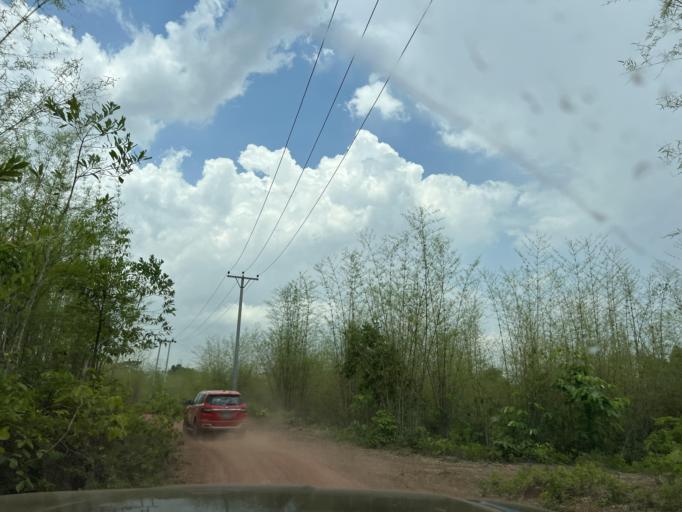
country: MM
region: Yangon
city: Twante
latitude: 16.5696
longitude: 95.9285
